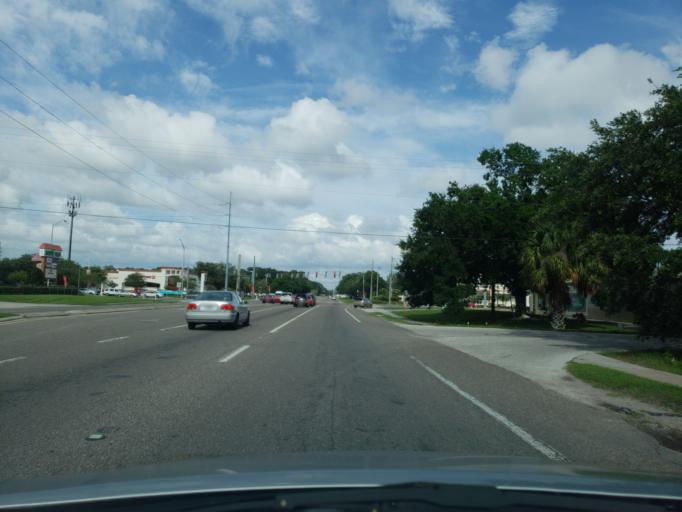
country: US
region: Florida
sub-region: Hillsborough County
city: Egypt Lake-Leto
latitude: 28.0070
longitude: -82.5063
